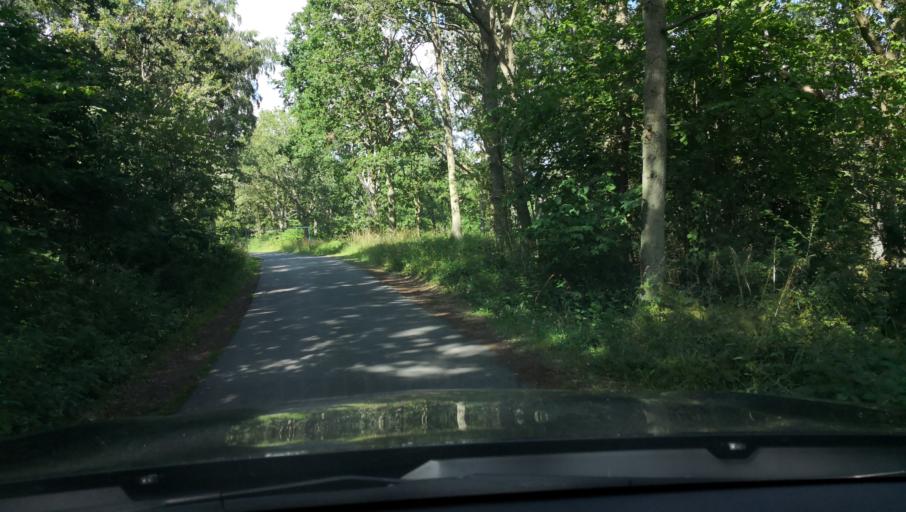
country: SE
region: Skane
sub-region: Ystads Kommun
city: Kopingebro
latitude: 55.3842
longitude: 14.1467
